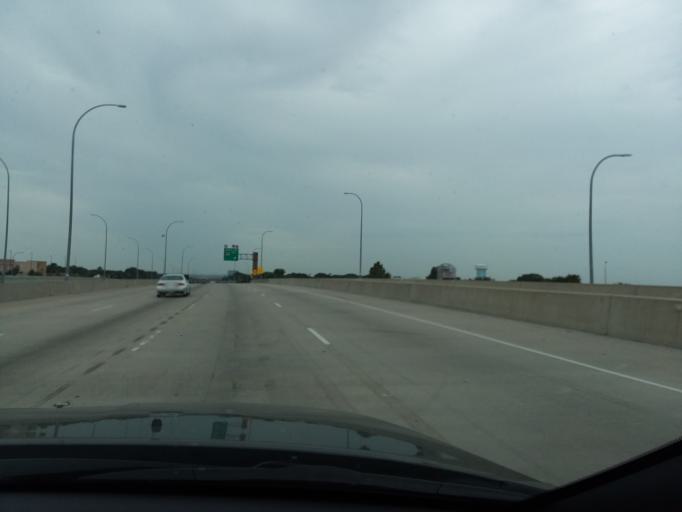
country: US
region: Texas
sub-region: Dallas County
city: Addison
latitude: 32.9248
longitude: -96.8405
